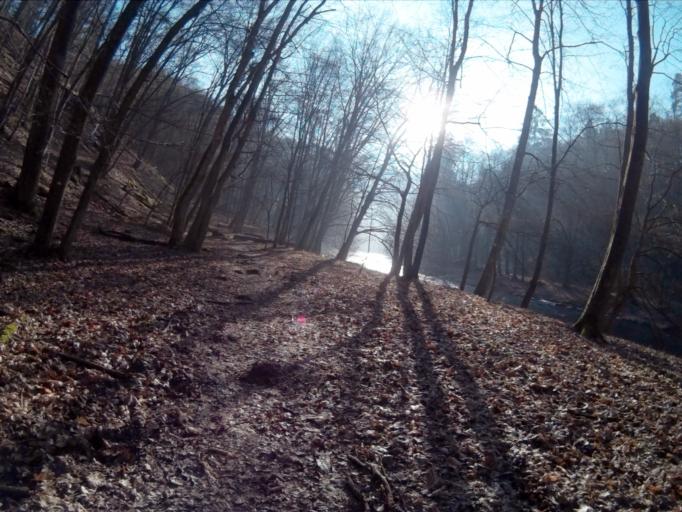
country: CZ
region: Vysocina
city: Namest' nad Oslavou
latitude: 49.1684
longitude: 16.1707
